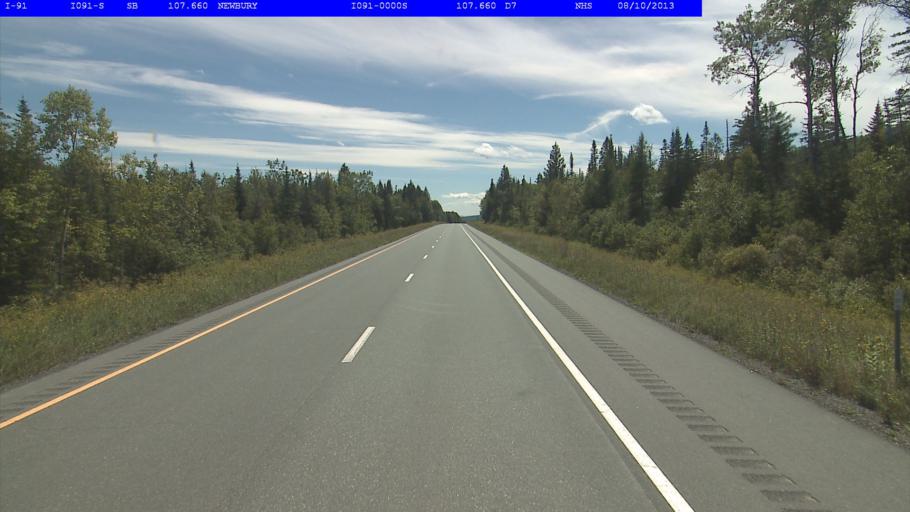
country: US
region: New Hampshire
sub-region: Grafton County
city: Woodsville
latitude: 44.1240
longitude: -72.1051
